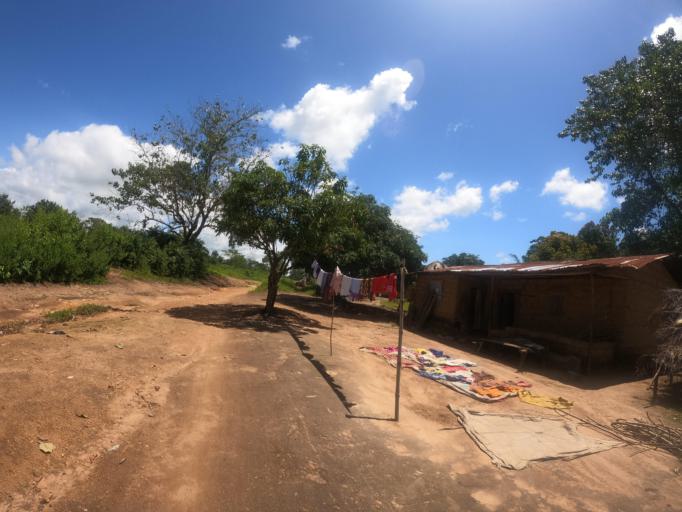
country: SL
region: Northern Province
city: Makeni
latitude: 8.8481
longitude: -12.1147
